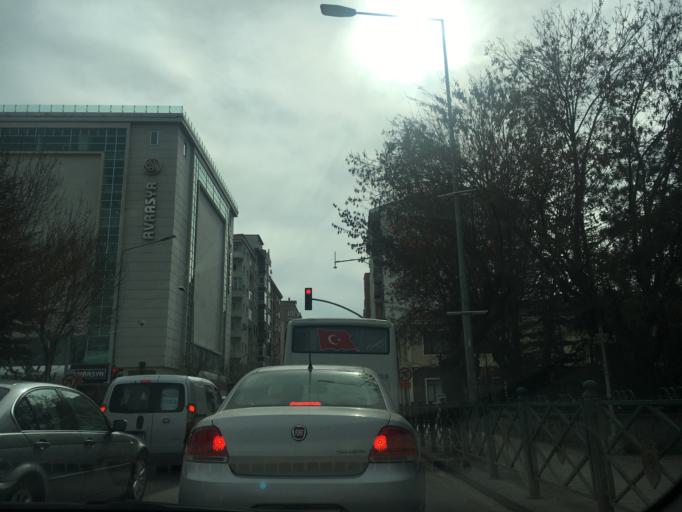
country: TR
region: Eskisehir
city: Eskisehir
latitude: 39.7698
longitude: 30.5167
